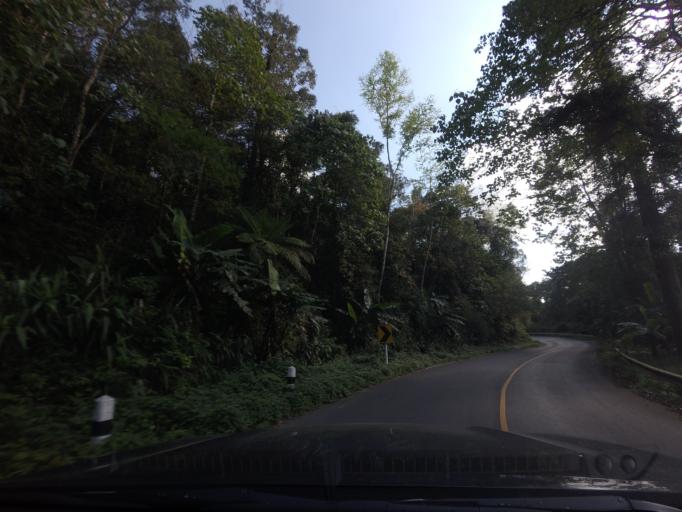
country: TH
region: Phetchabun
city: Lom Kao
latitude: 16.9317
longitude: 101.0708
